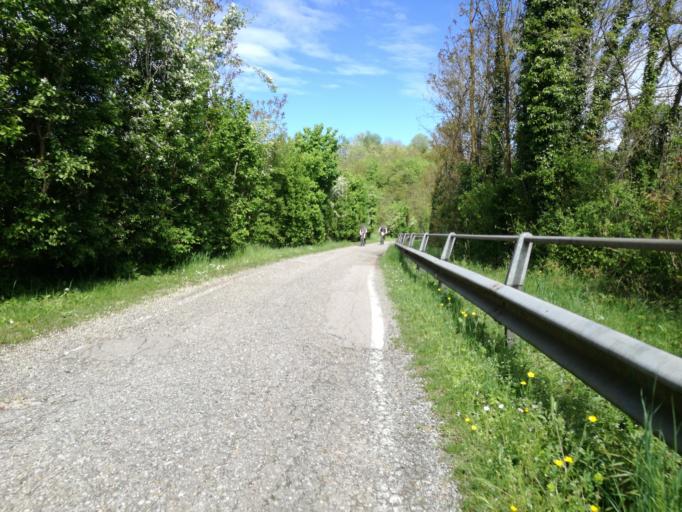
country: IT
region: Lombardy
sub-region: Provincia di Monza e Brianza
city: Porto d'Adda
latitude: 45.6602
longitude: 9.4866
